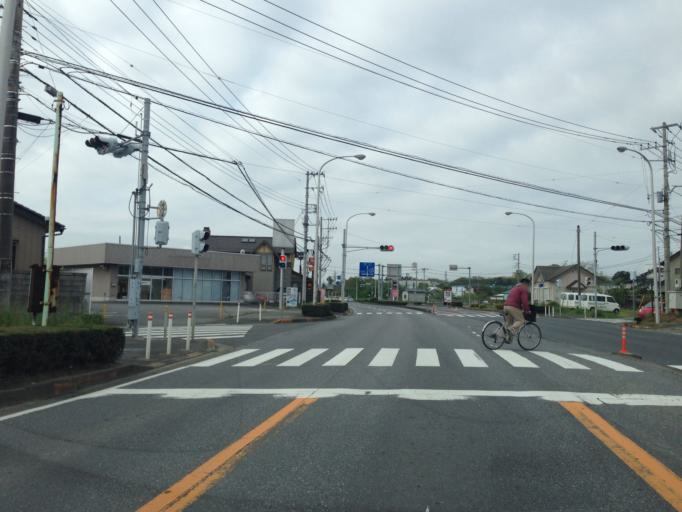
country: JP
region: Ibaraki
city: Tsukuba
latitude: 36.1367
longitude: 140.0801
